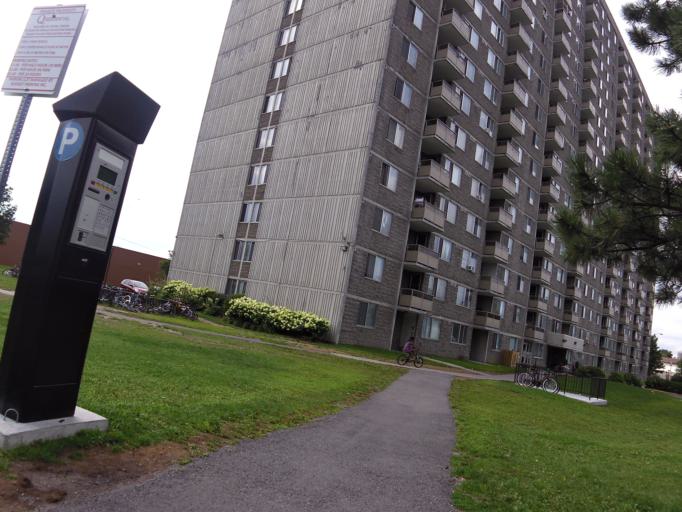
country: CA
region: Ontario
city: Ottawa
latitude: 45.4278
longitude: -75.6358
